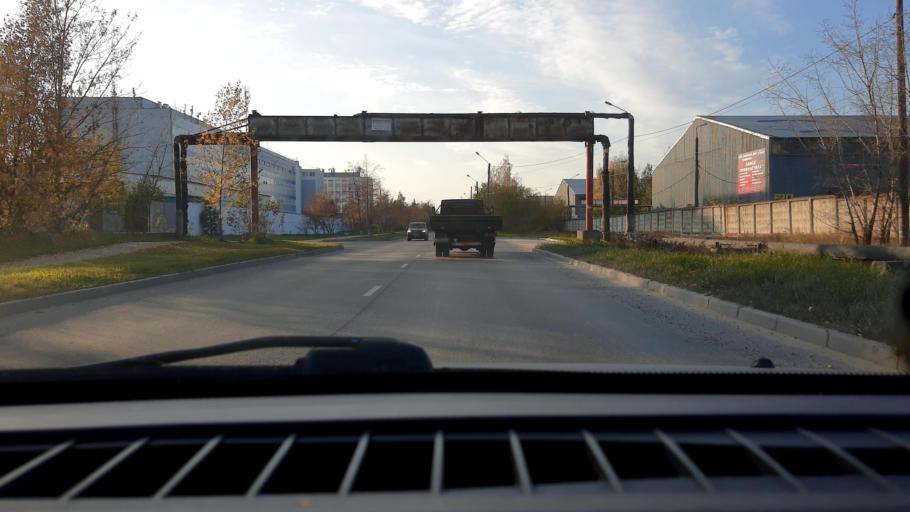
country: RU
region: Nizjnij Novgorod
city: Gorbatovka
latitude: 56.3494
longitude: 43.8110
